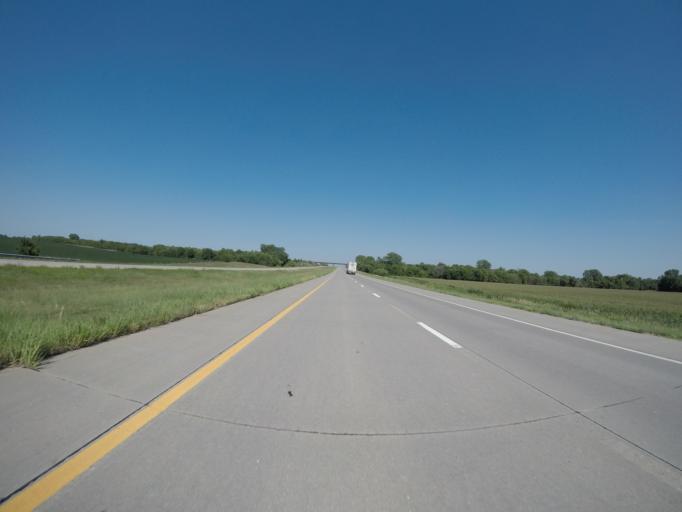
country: US
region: Kansas
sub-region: Dickinson County
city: Chapman
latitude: 38.9933
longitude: -96.9692
